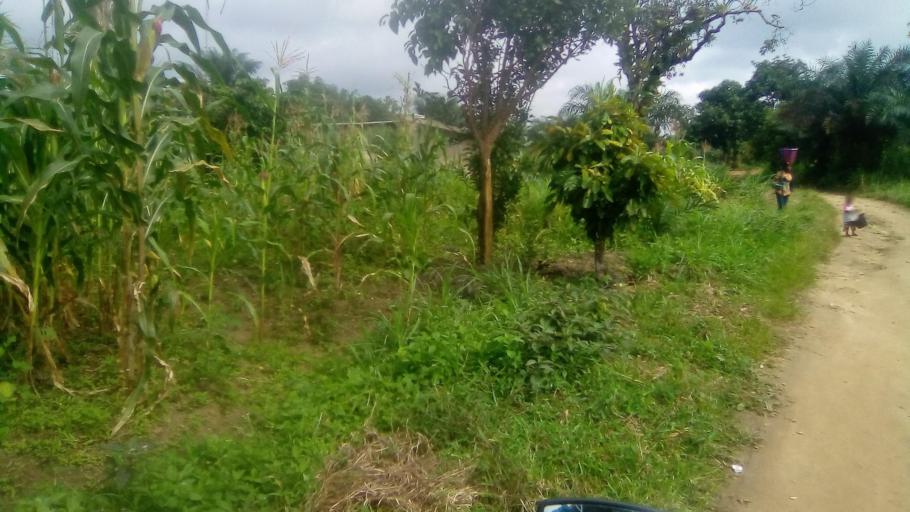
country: SL
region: Eastern Province
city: Kailahun
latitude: 8.2837
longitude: -10.5608
